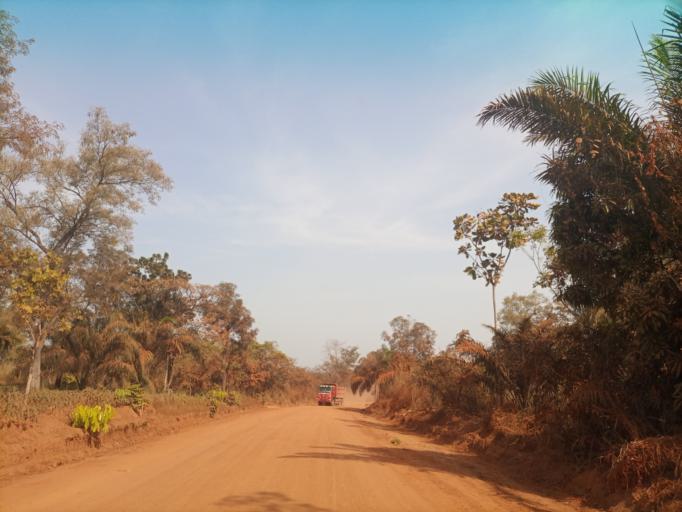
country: NG
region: Enugu
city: Eha Amufu
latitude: 6.6743
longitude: 7.7300
